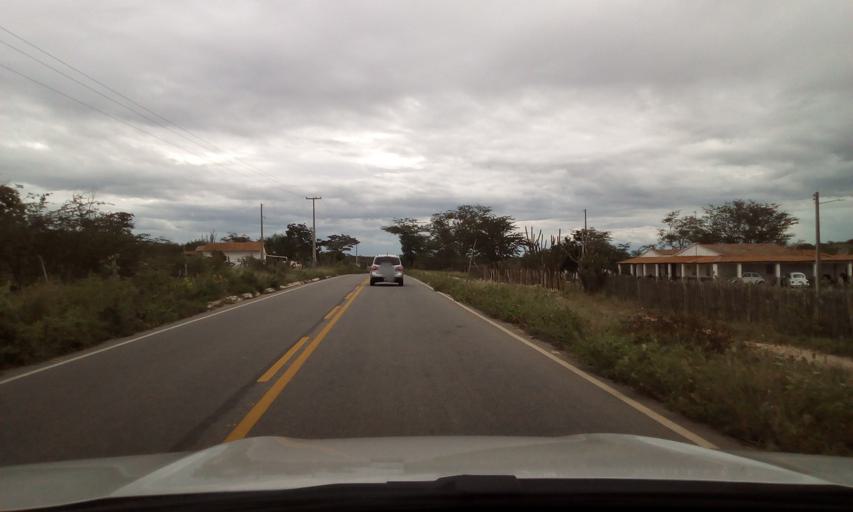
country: BR
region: Paraiba
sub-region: Picui
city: Picui
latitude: -6.5600
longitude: -36.2874
